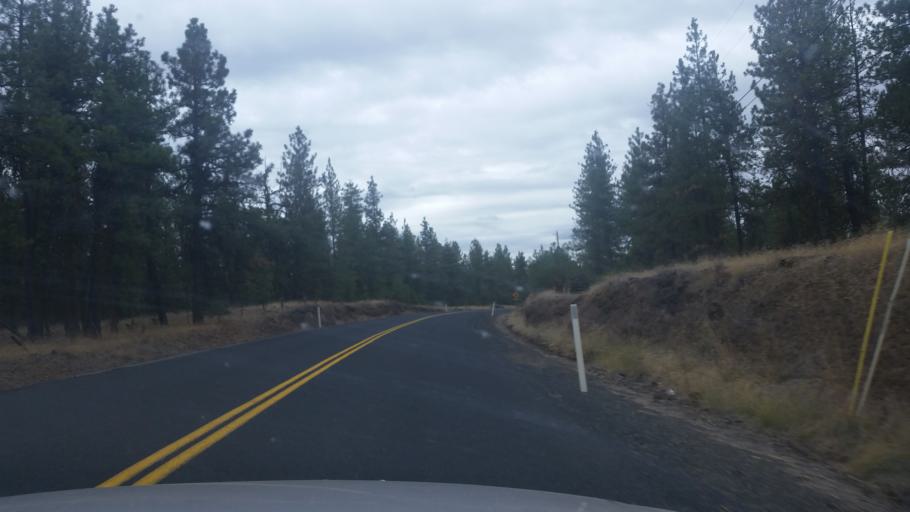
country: US
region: Washington
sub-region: Spokane County
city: Medical Lake
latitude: 47.4951
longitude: -117.7707
